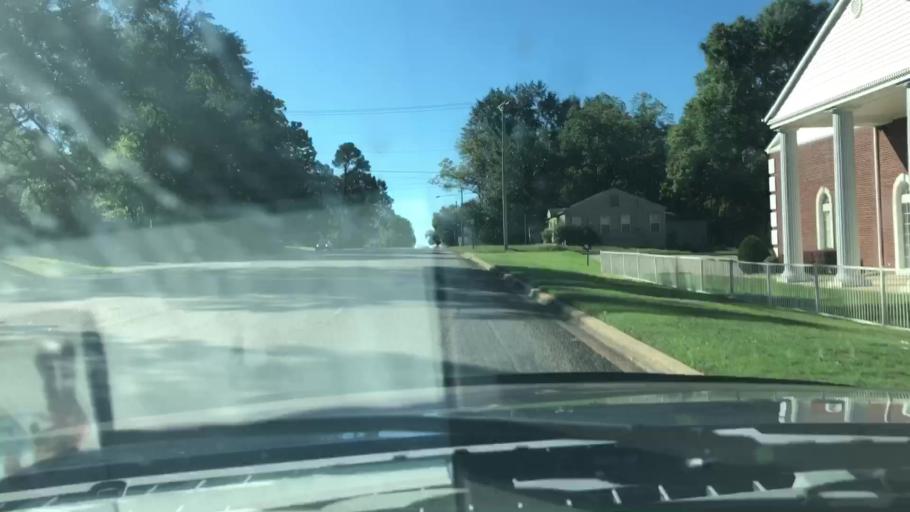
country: US
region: Arkansas
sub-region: Miller County
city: Texarkana
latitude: 33.4448
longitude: -94.0531
